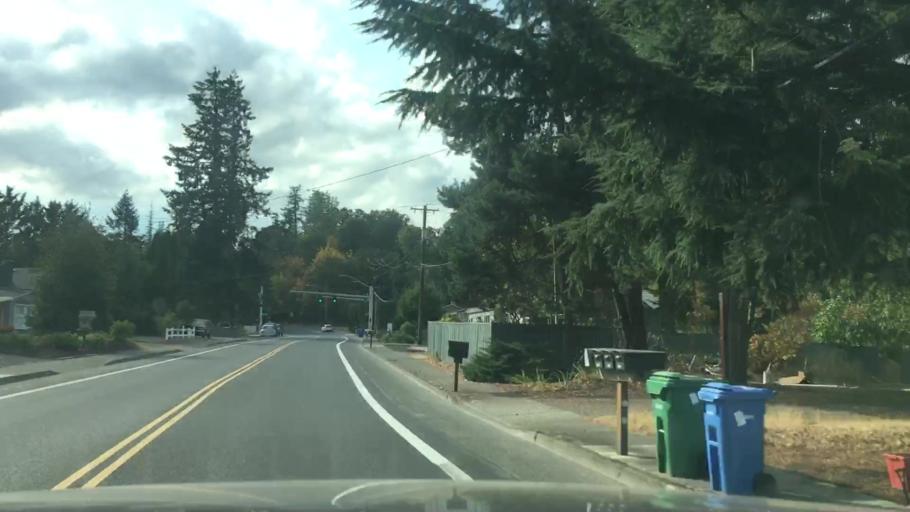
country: US
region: Oregon
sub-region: Lane County
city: Eugene
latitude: 44.0841
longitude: -123.0926
